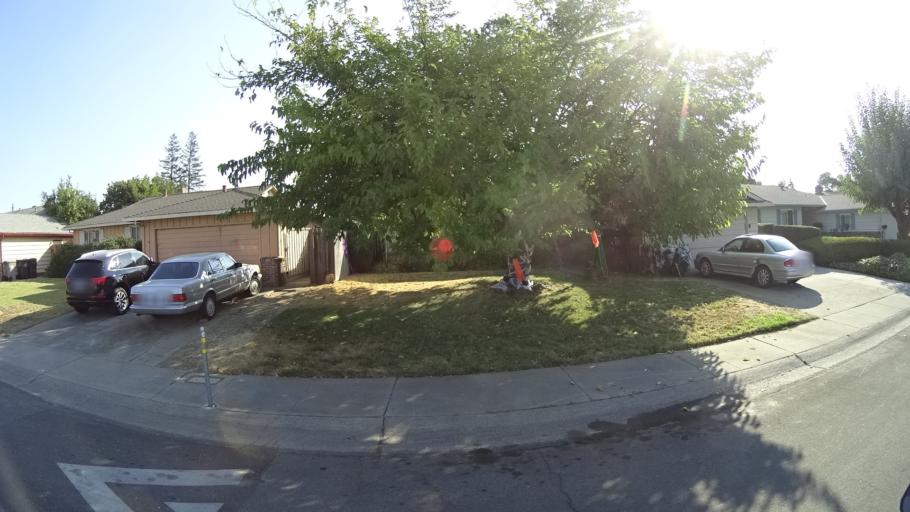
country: US
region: California
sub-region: Sacramento County
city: Parkway
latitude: 38.4933
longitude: -121.5011
